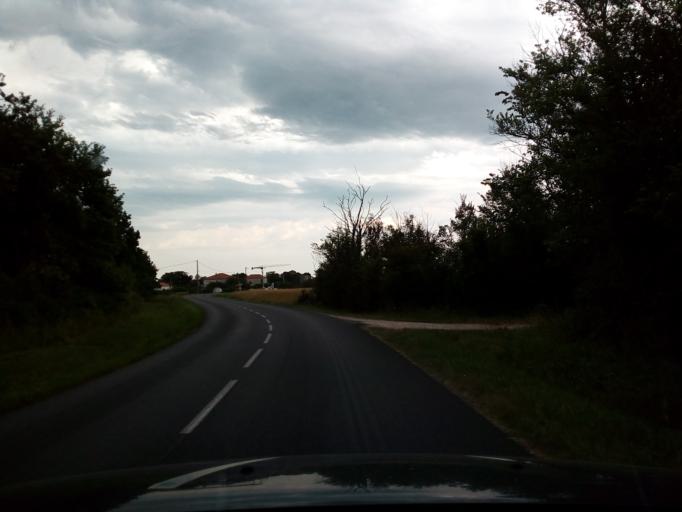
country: FR
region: Poitou-Charentes
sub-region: Departement de la Charente-Maritime
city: Dolus-d'Oleron
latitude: 45.9355
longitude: -1.3118
